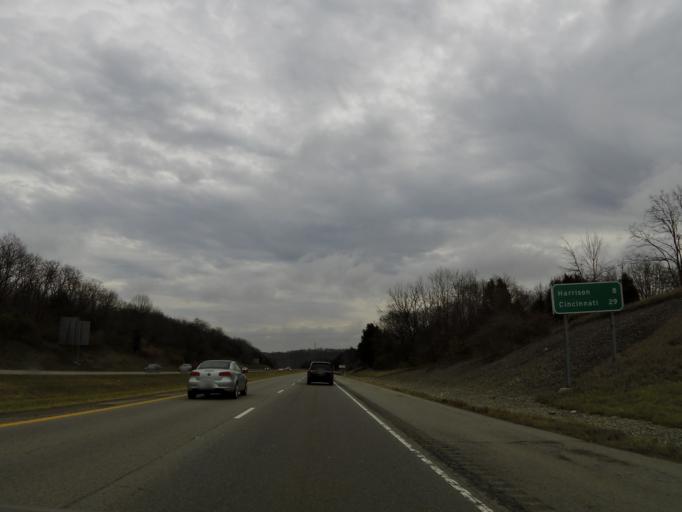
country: US
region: Indiana
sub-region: Dearborn County
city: Bright
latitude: 39.2749
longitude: -84.9463
